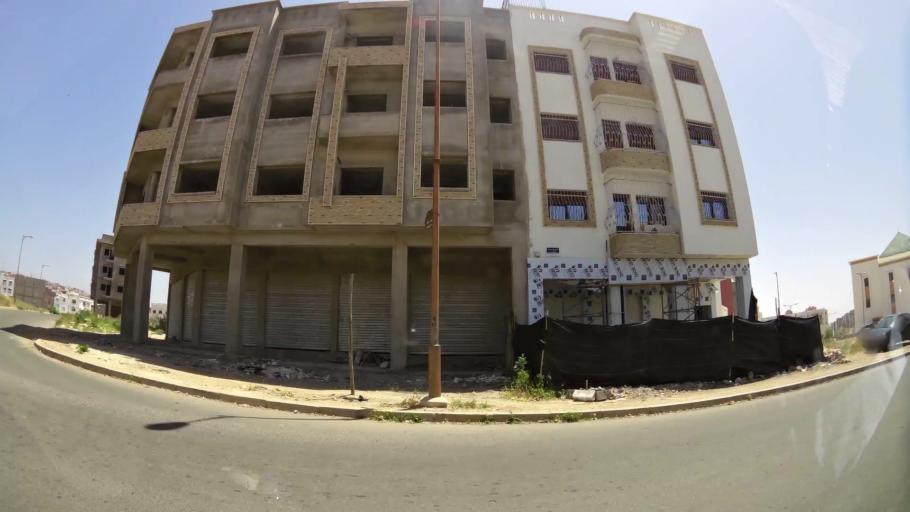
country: MA
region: Oued ed Dahab-Lagouira
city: Dakhla
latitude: 30.4384
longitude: -9.5562
